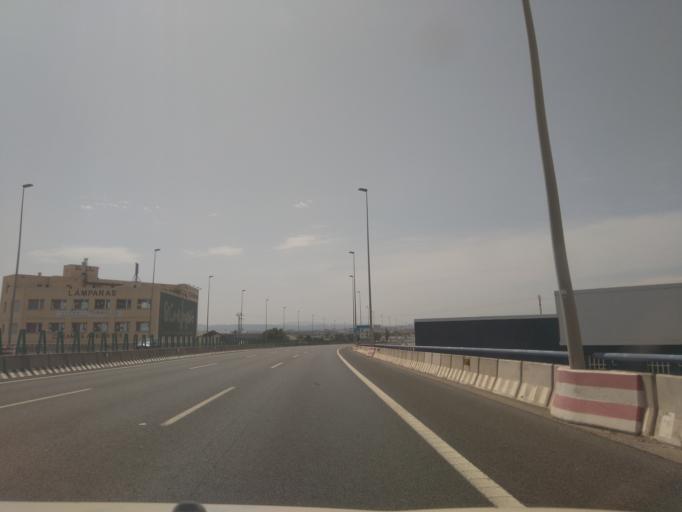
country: ES
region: Valencia
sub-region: Provincia de Valencia
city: Beniparrell
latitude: 39.3755
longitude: -0.4148
